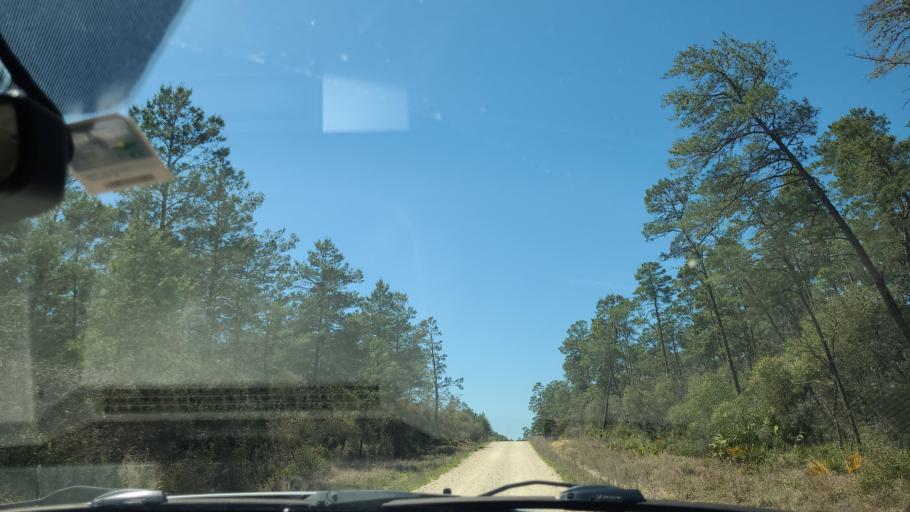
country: US
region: Florida
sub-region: Putnam County
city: Interlachen
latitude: 29.4283
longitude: -81.8975
